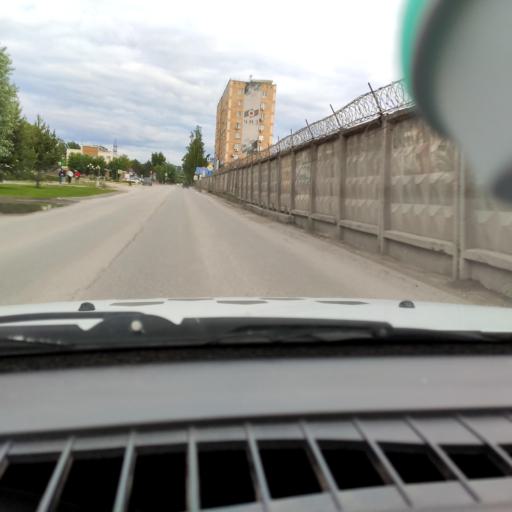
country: RU
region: Perm
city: Chusovoy
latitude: 58.2964
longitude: 57.8120
